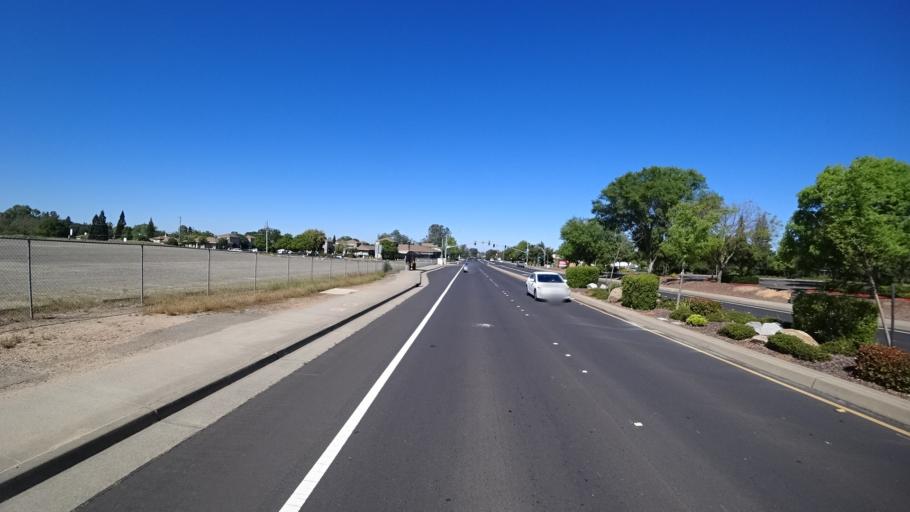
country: US
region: California
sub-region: Placer County
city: Rocklin
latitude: 38.7885
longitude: -121.2136
